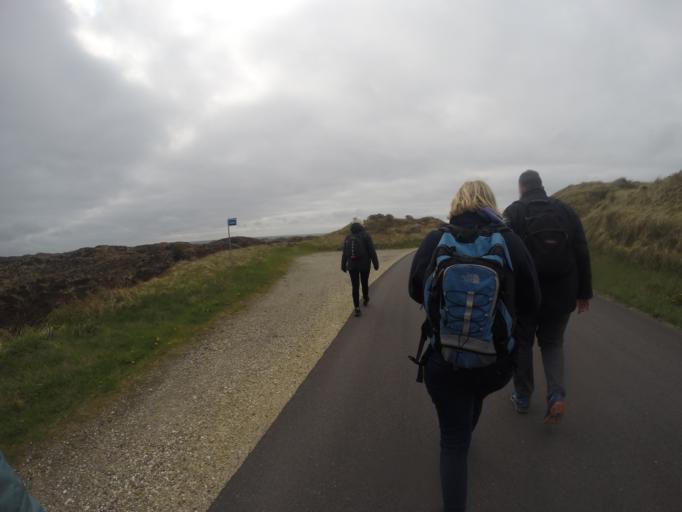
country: DK
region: North Denmark
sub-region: Thisted Kommune
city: Hurup
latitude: 56.9248
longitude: 8.3475
